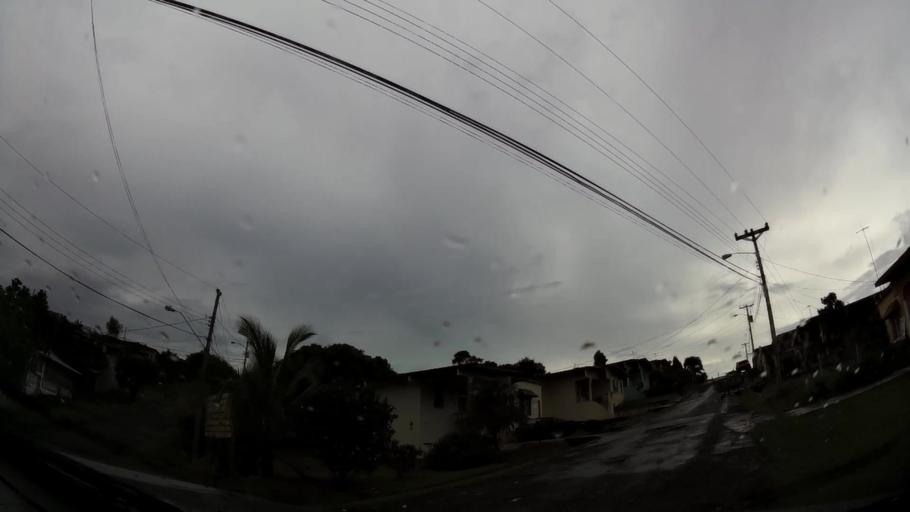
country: PA
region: Veraguas
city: Santiago de Veraguas
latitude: 8.0901
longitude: -80.9899
